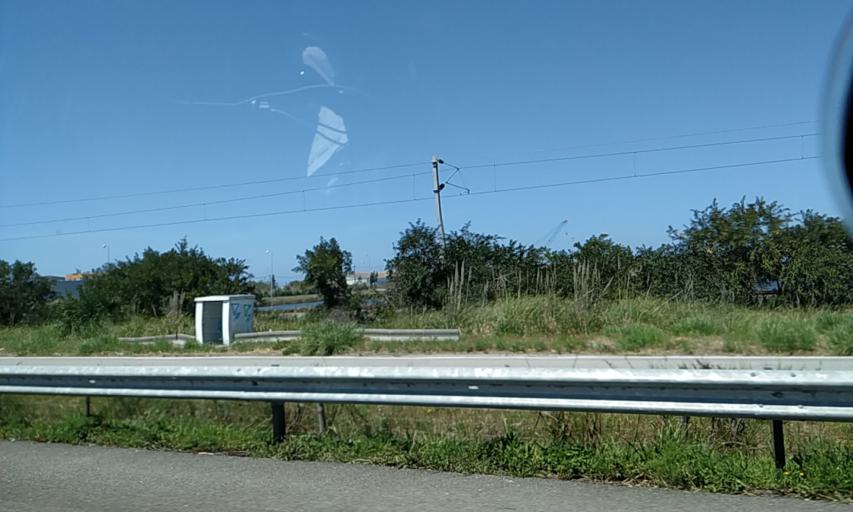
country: PT
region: Aveiro
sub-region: Ilhavo
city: Gafanha da Nazare
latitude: 40.6338
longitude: -8.6795
